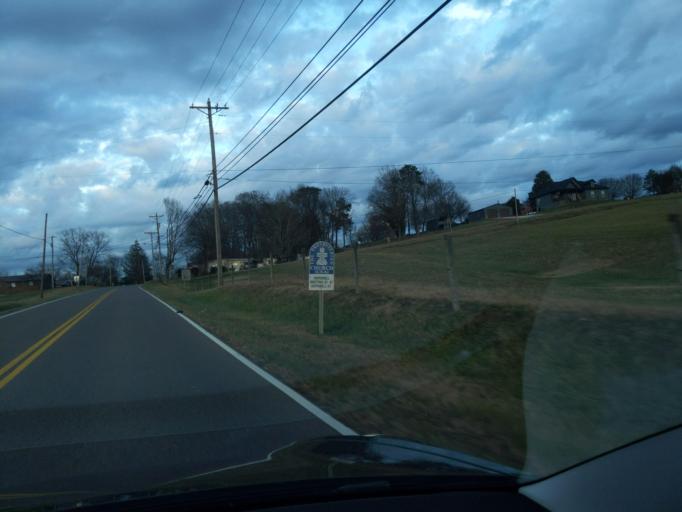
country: US
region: Tennessee
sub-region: Jefferson County
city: Dandridge
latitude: 36.0121
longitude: -83.4217
